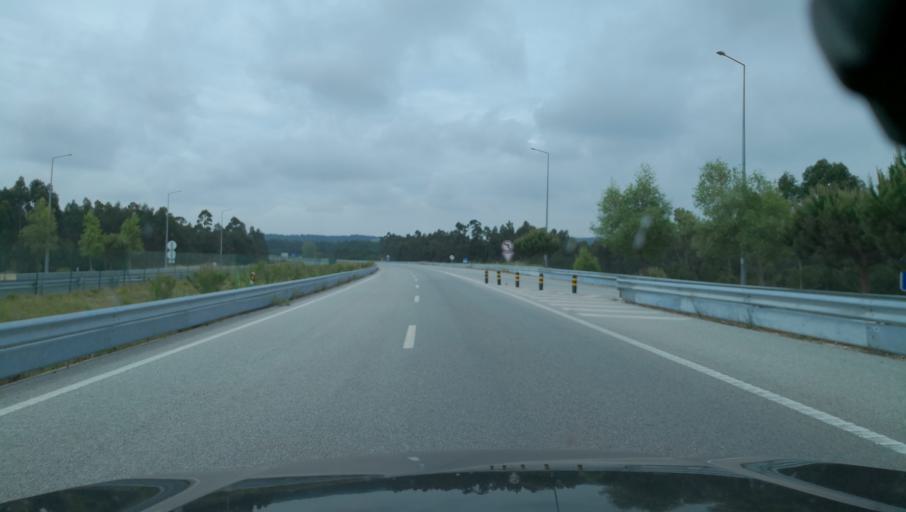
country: PT
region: Coimbra
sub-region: Figueira da Foz
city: Alhadas
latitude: 40.2119
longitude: -8.8113
